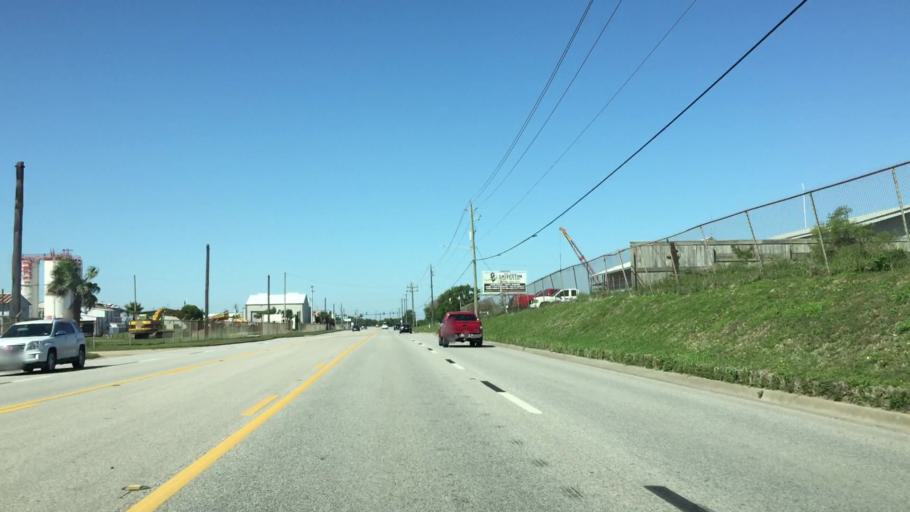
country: US
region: Texas
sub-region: Galveston County
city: Galveston
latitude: 29.2937
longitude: -94.8563
